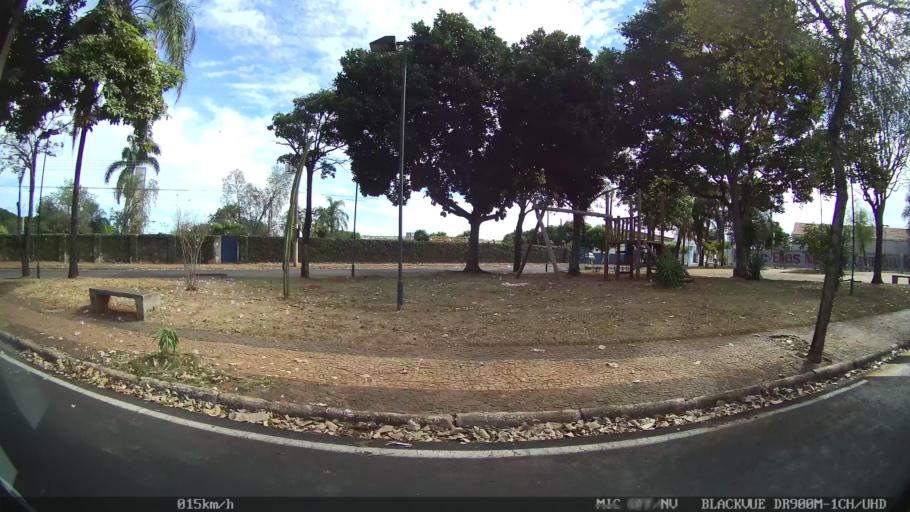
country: BR
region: Sao Paulo
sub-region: Catanduva
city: Catanduva
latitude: -21.1318
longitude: -48.9569
